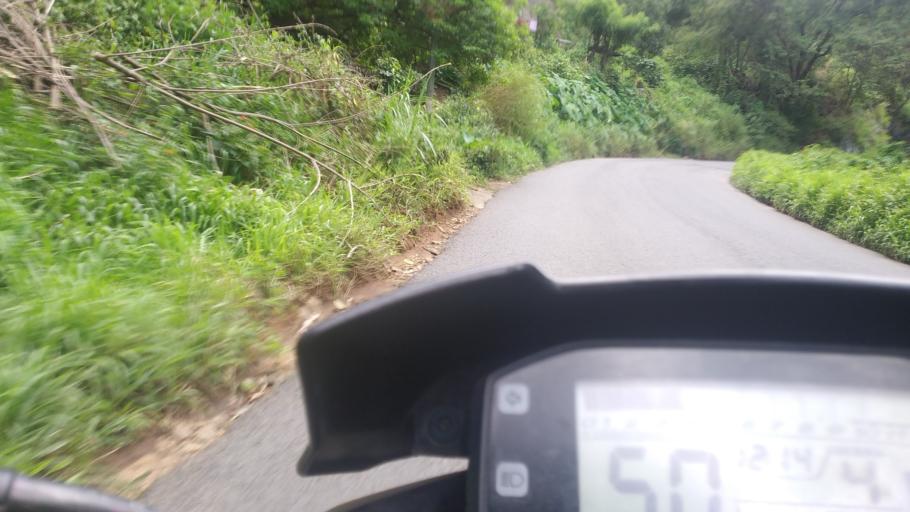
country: IN
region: Kerala
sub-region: Idukki
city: Munnar
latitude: 10.0154
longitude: 77.0048
